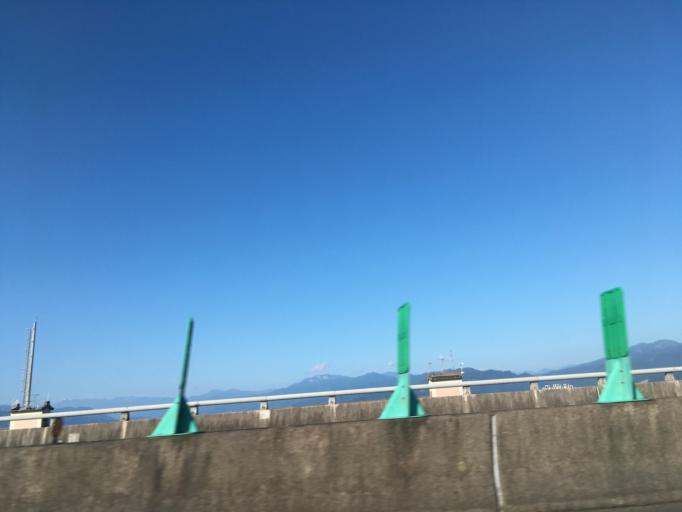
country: TW
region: Taiwan
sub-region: Yilan
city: Yilan
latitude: 24.7347
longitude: 121.7821
